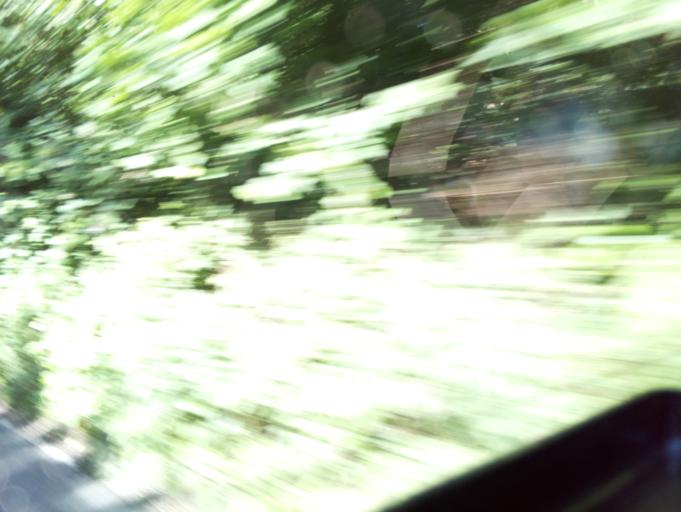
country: GB
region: England
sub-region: Gloucestershire
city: Lydbrook
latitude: 51.8481
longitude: -2.5979
